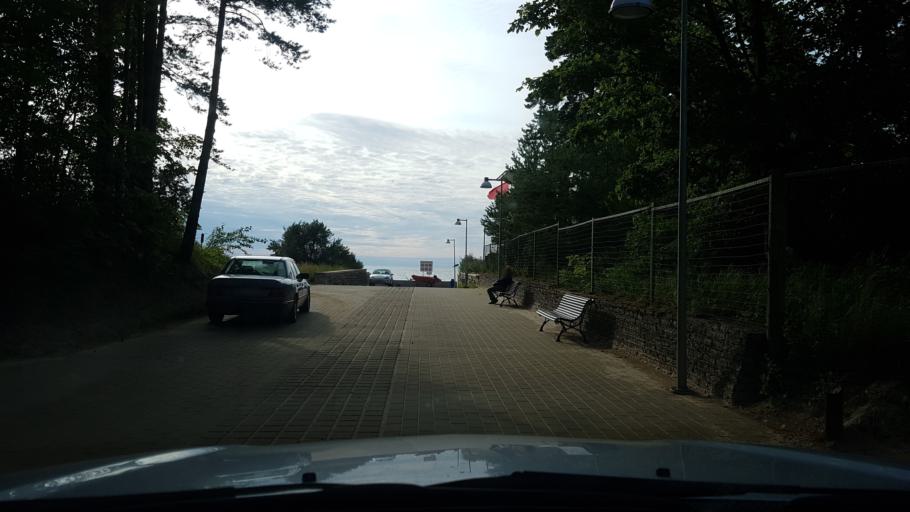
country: EE
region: Ida-Virumaa
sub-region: Narva-Joesuu linn
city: Narva-Joesuu
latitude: 59.4610
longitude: 28.0340
